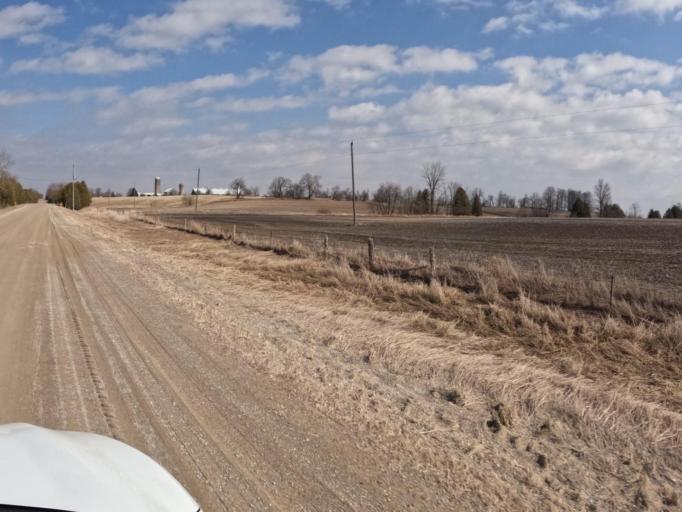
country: CA
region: Ontario
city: Orangeville
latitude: 43.9193
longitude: -80.2551
